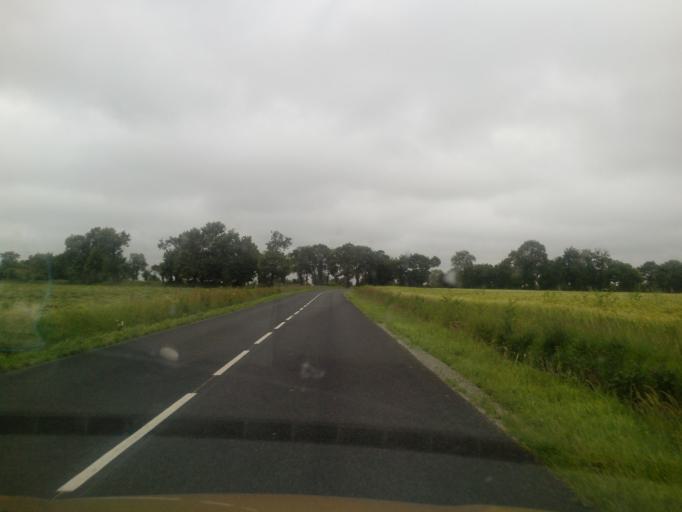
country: FR
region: Brittany
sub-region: Departement d'Ille-et-Vilaine
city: Sens-de-Bretagne
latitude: 48.3357
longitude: -1.5195
